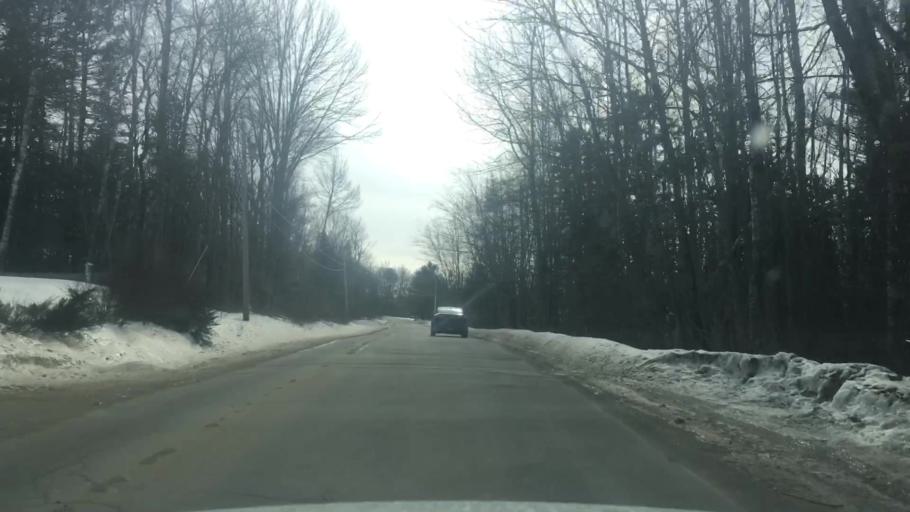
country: US
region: Maine
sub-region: Hancock County
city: Orland
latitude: 44.5881
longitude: -68.7258
